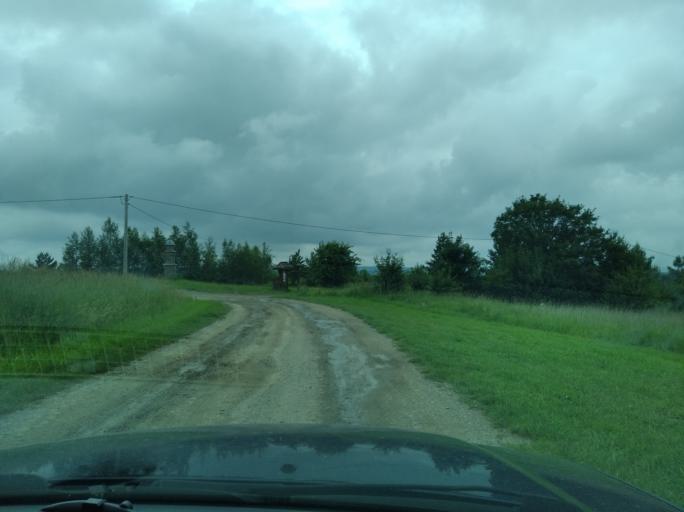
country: PL
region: Subcarpathian Voivodeship
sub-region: Powiat jaroslawski
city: Pruchnik
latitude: 49.8871
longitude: 22.5166
